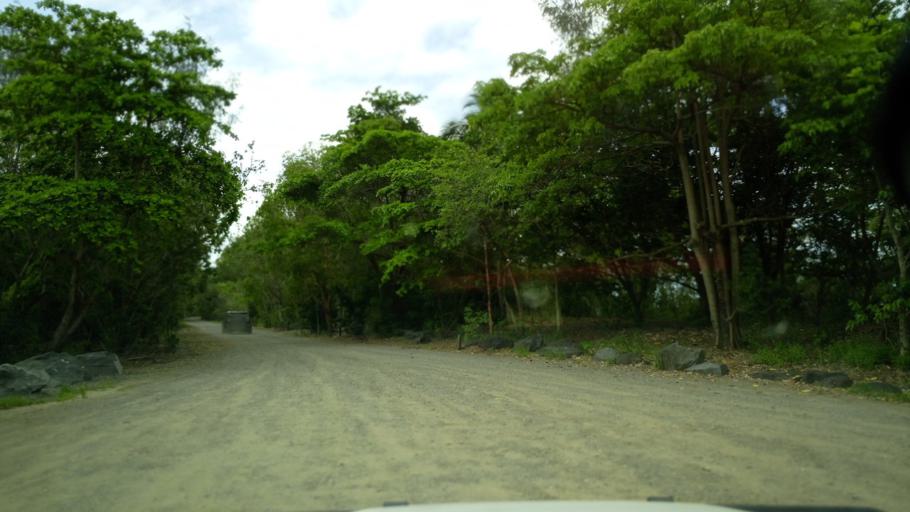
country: AU
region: Queensland
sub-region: Cairns
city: Cairns
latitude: -16.8614
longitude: 145.7600
